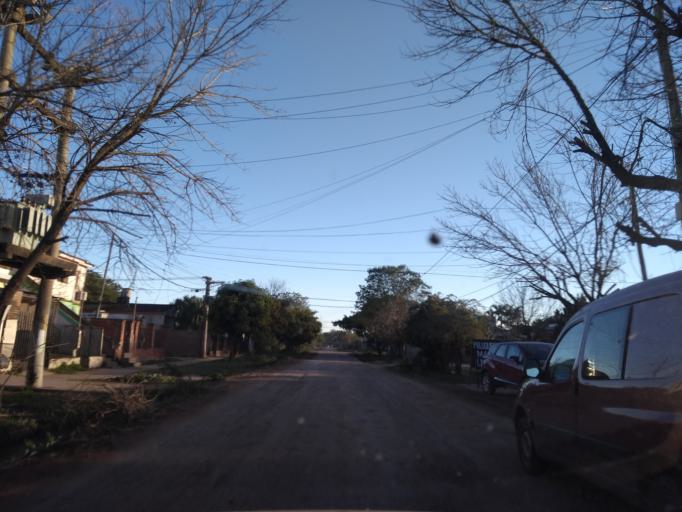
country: AR
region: Chaco
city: Puerto Vilelas
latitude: -27.4982
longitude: -58.9584
